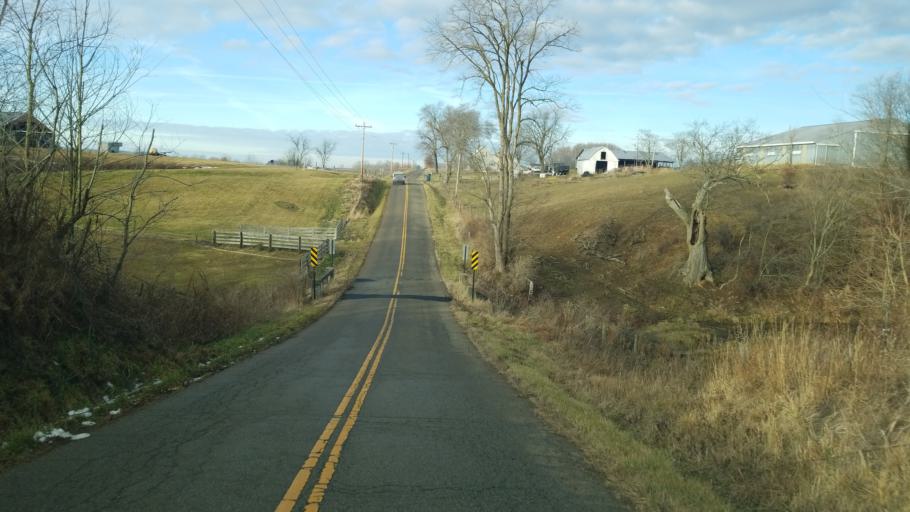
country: US
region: Ohio
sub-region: Knox County
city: Gambier
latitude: 40.3137
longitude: -82.3345
